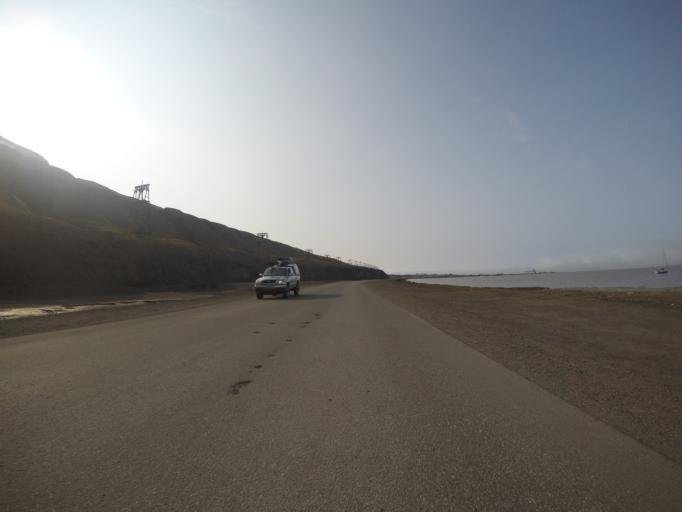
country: SJ
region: Svalbard
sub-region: Spitsbergen
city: Longyearbyen
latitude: 78.2293
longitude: 15.5903
